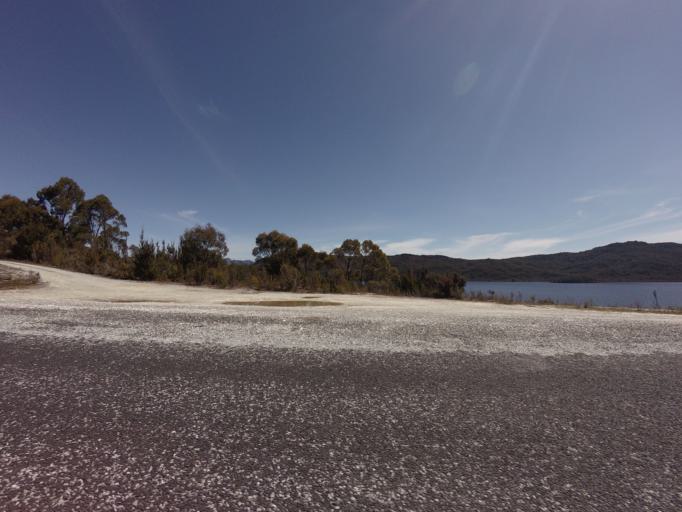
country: AU
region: Tasmania
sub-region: Huon Valley
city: Geeveston
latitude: -42.8331
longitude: 146.1254
